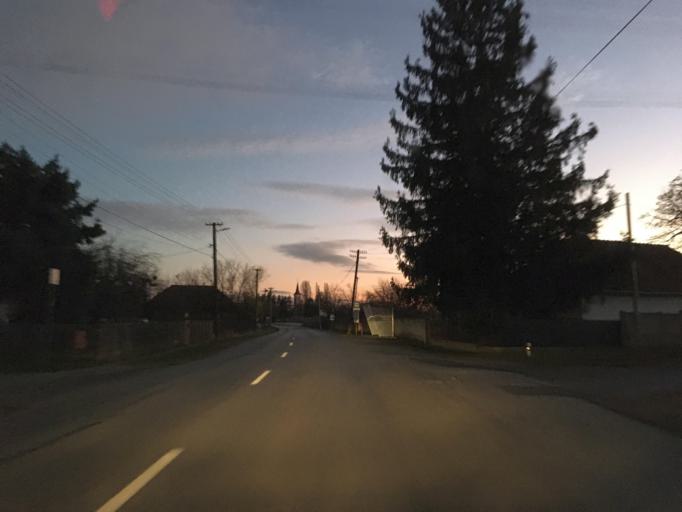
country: SK
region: Nitriansky
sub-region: Okres Komarno
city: Hurbanovo
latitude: 47.9089
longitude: 18.1352
